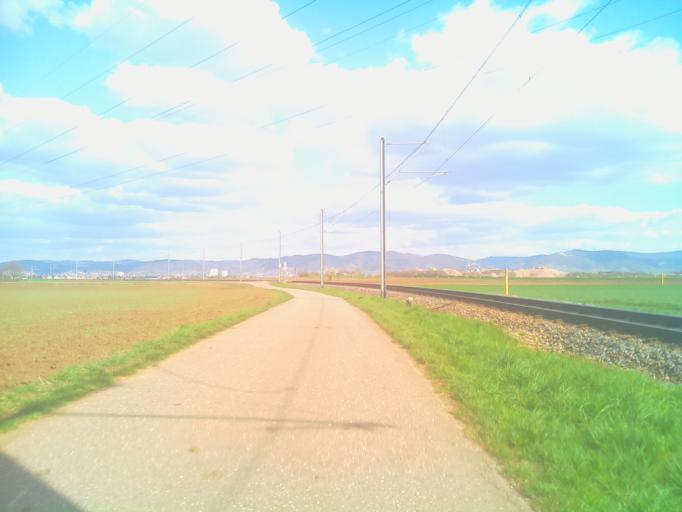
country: DE
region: Baden-Wuerttemberg
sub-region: Karlsruhe Region
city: Ilvesheim
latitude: 49.4955
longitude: 8.5668
